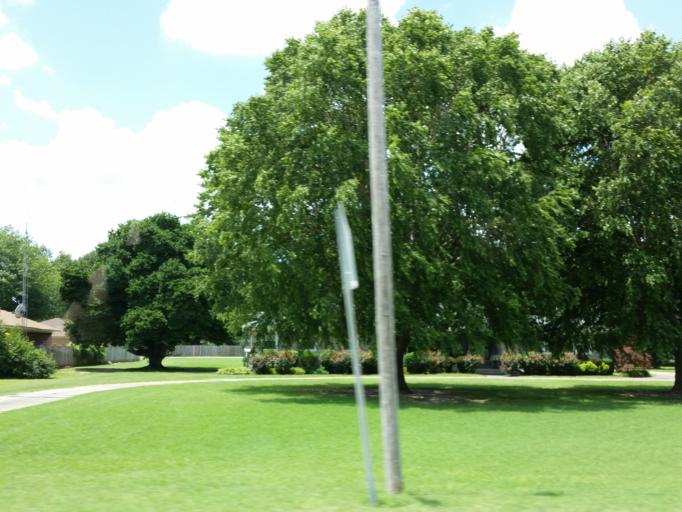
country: US
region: Tennessee
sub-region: Lake County
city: Ridgely
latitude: 36.2694
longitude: -89.4781
